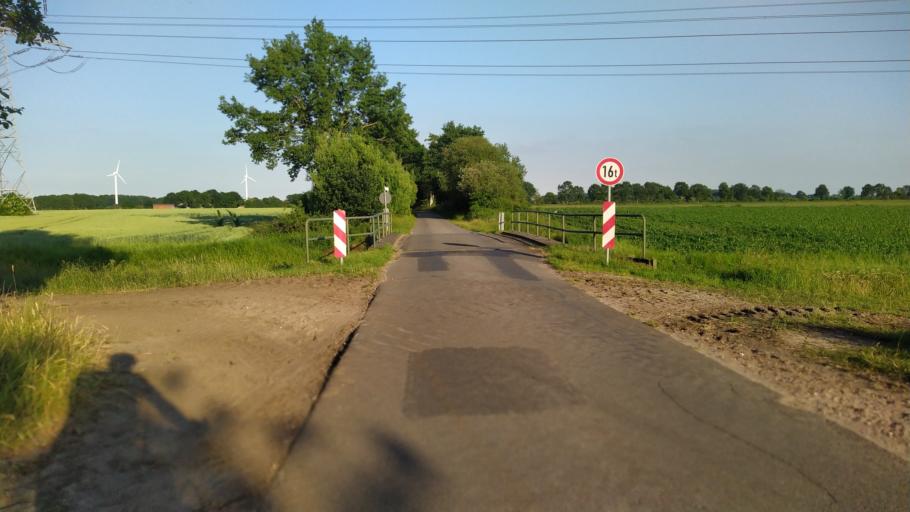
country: DE
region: Lower Saxony
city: Alfstedt
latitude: 53.5587
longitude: 9.0376
